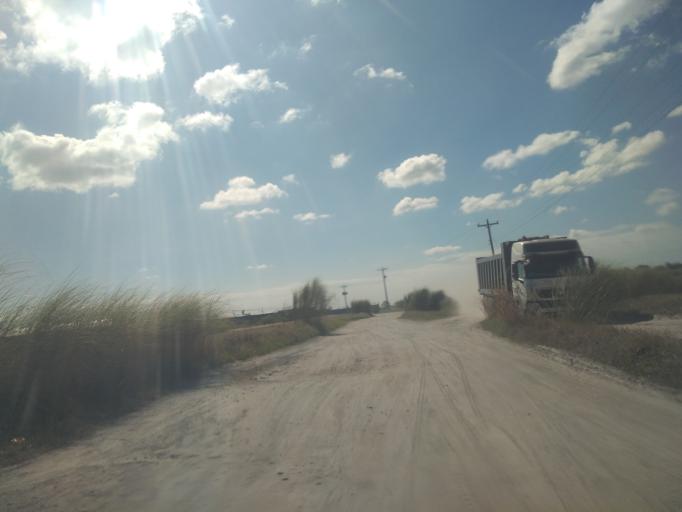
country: PH
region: Central Luzon
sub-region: Province of Pampanga
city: Balas
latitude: 15.0671
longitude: 120.5913
